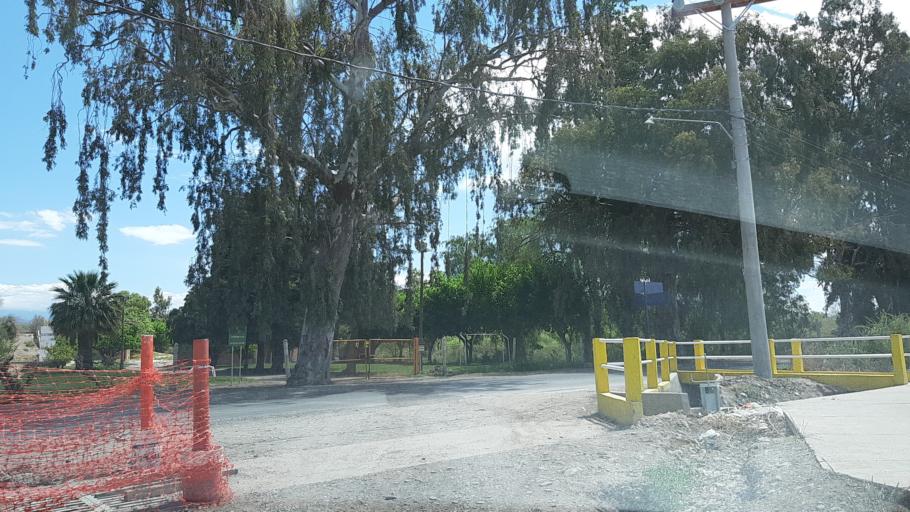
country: AR
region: San Juan
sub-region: Departamento de Rivadavia
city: Rivadavia
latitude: -31.5561
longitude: -68.6099
